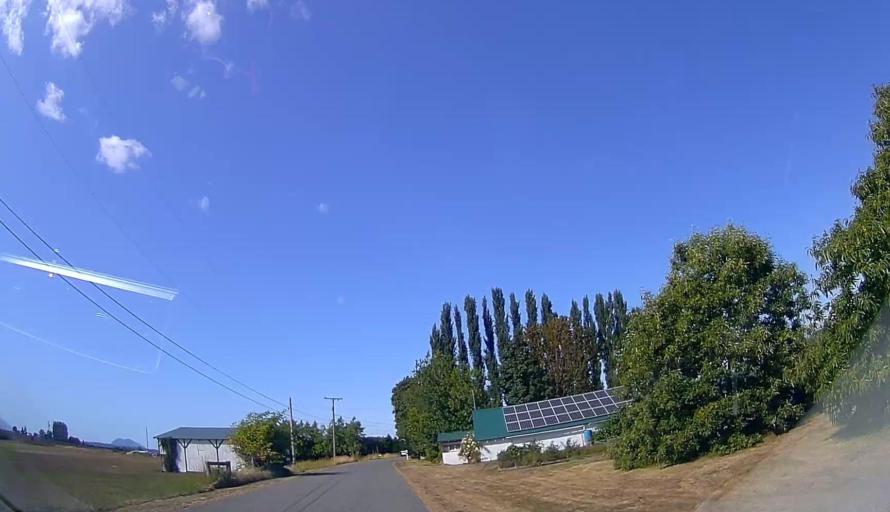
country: US
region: Washington
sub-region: Skagit County
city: Burlington
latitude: 48.5185
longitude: -122.4331
